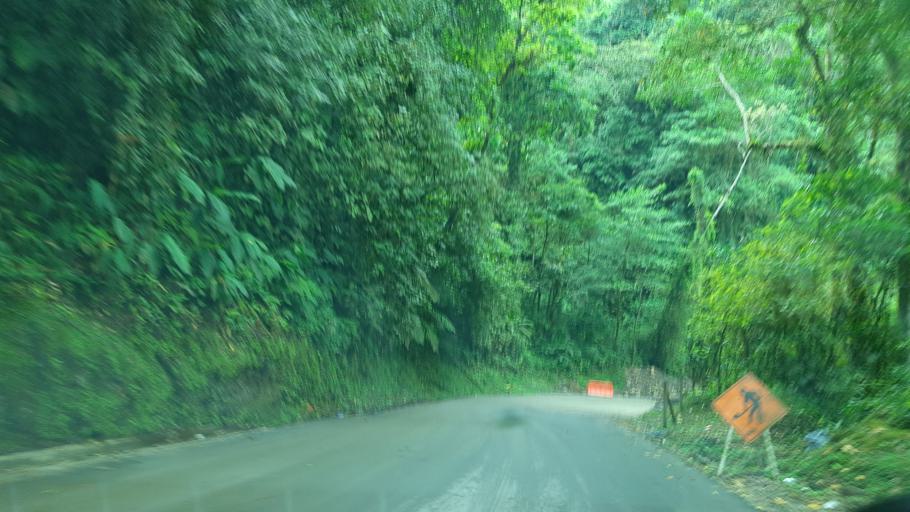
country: CO
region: Boyaca
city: Santa Maria
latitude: 4.8753
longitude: -73.2501
